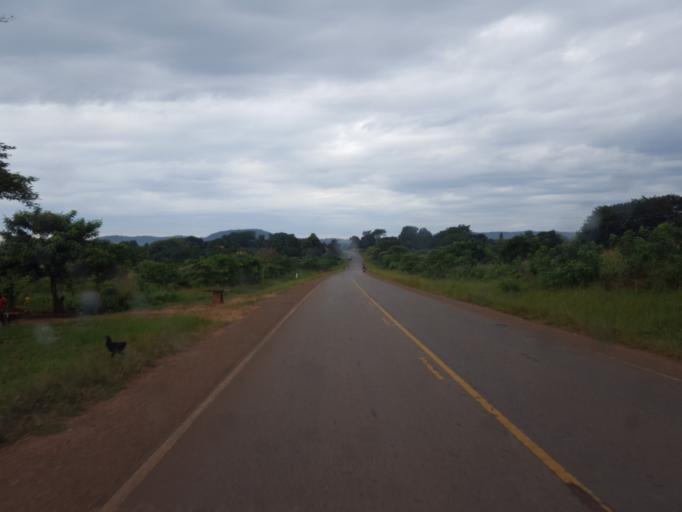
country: UG
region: Central Region
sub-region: Kiboga District
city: Kiboga
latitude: 1.0050
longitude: 31.6974
